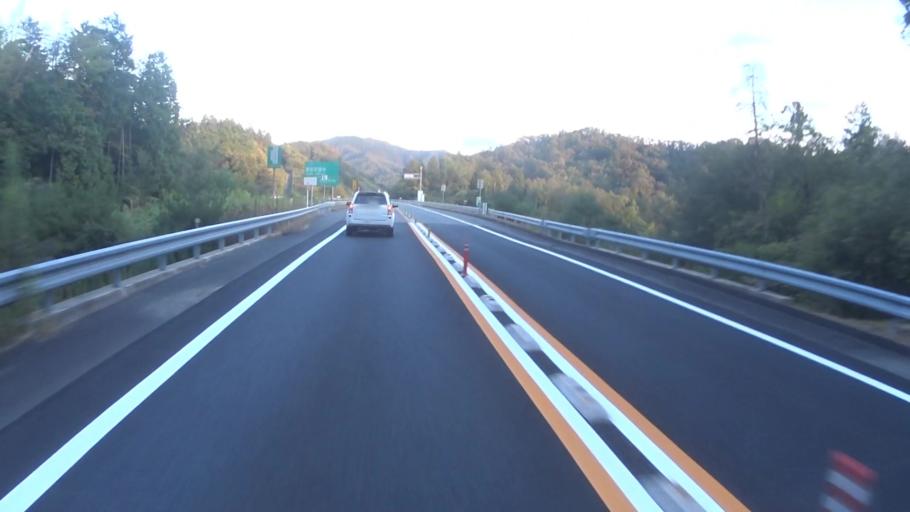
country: JP
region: Kyoto
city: Ayabe
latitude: 35.3447
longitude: 135.2985
